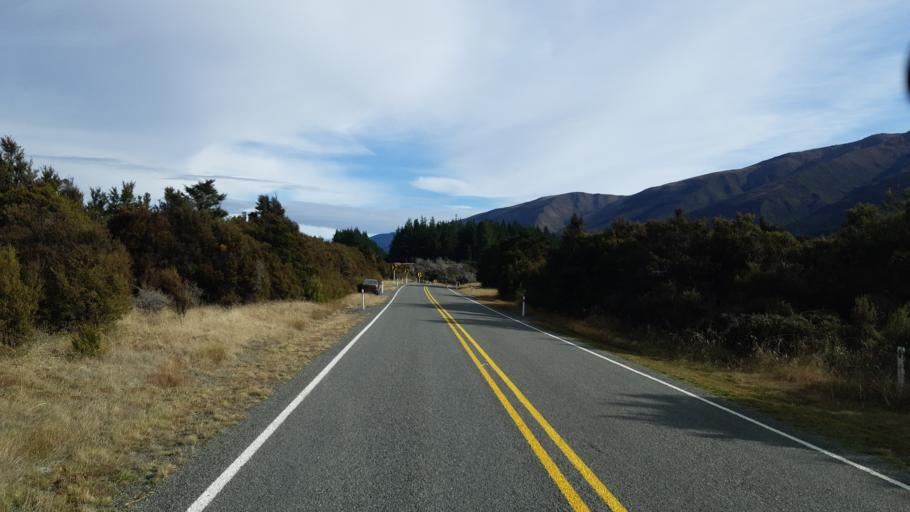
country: NZ
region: Tasman
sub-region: Tasman District
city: Wakefield
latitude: -41.7147
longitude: 173.0853
